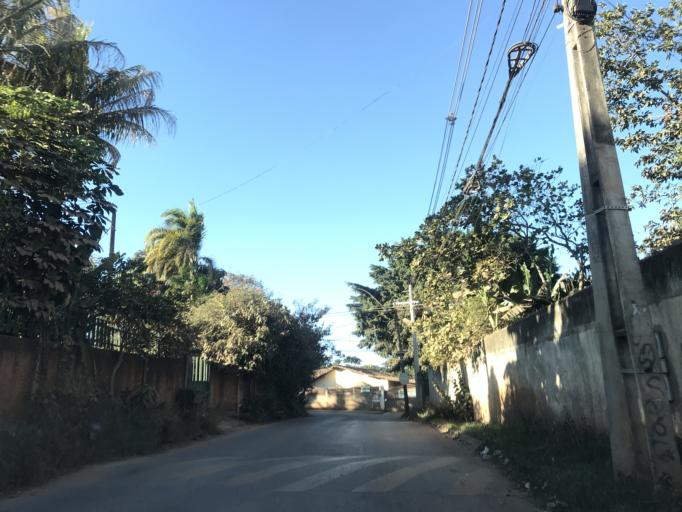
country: BR
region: Federal District
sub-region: Brasilia
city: Brasilia
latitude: -15.8802
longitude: -47.7789
